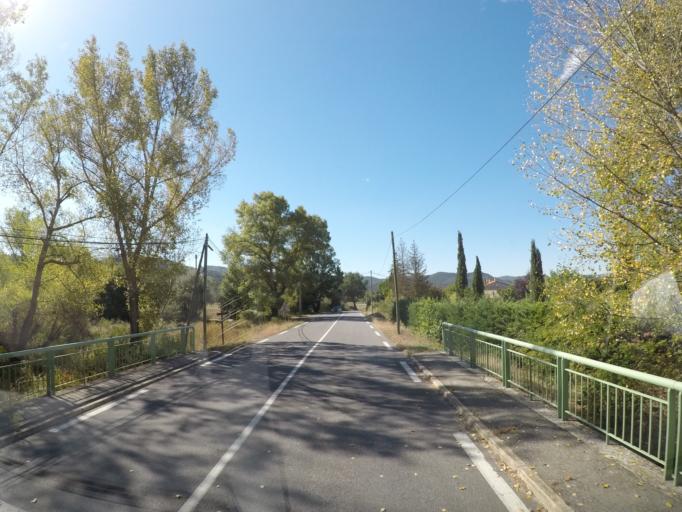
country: FR
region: Provence-Alpes-Cote d'Azur
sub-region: Departement des Alpes-de-Haute-Provence
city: Mallemoisson
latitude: 44.0474
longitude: 6.1626
